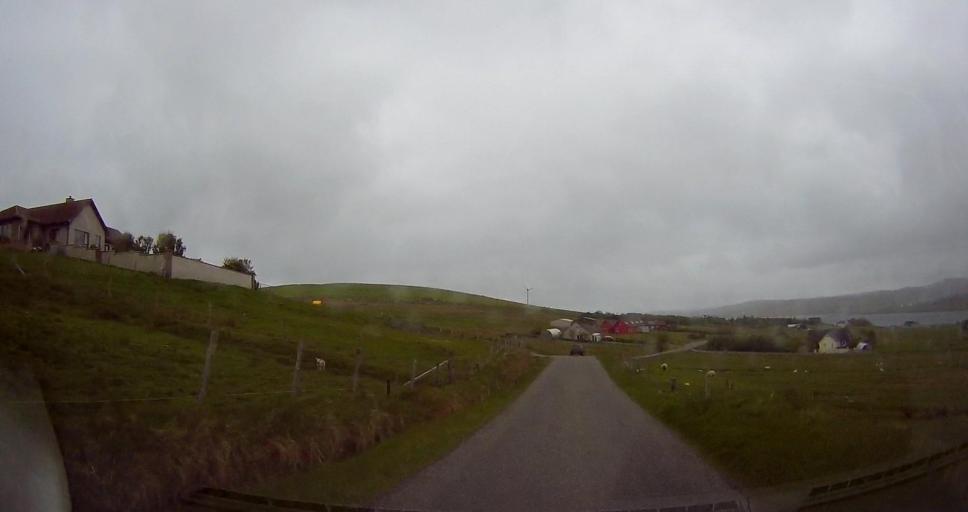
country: GB
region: Scotland
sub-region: Shetland Islands
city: Lerwick
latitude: 60.2815
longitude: -1.3885
